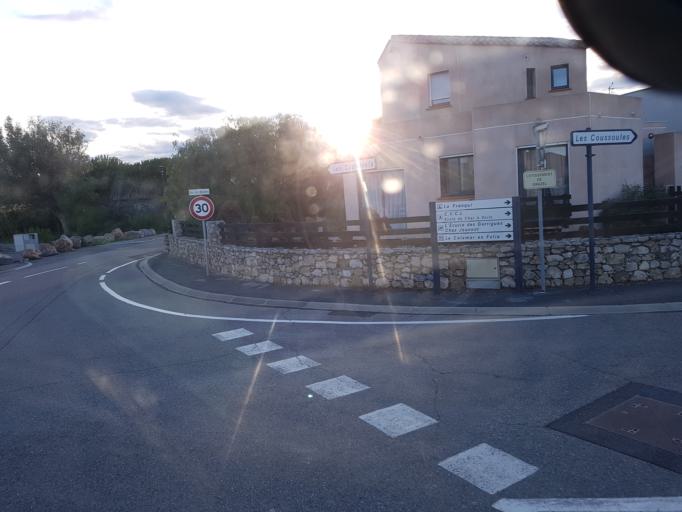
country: FR
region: Languedoc-Roussillon
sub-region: Departement de l'Aude
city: Leucate
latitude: 42.9374
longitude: 3.0278
